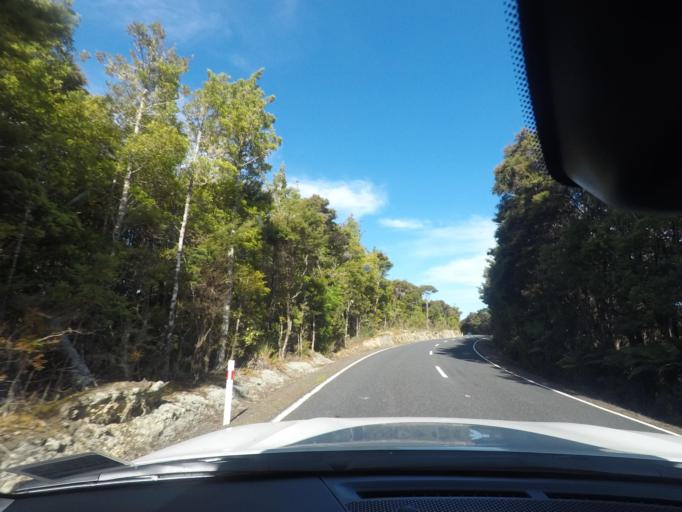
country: NZ
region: Northland
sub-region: Whangarei
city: Ngunguru
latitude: -35.6659
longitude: 174.4746
